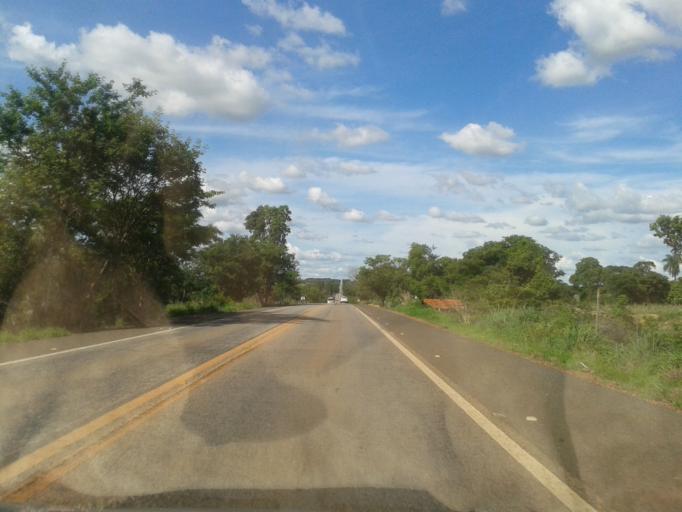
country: BR
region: Goias
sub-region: Mozarlandia
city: Mozarlandia
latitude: -15.0796
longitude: -50.6221
